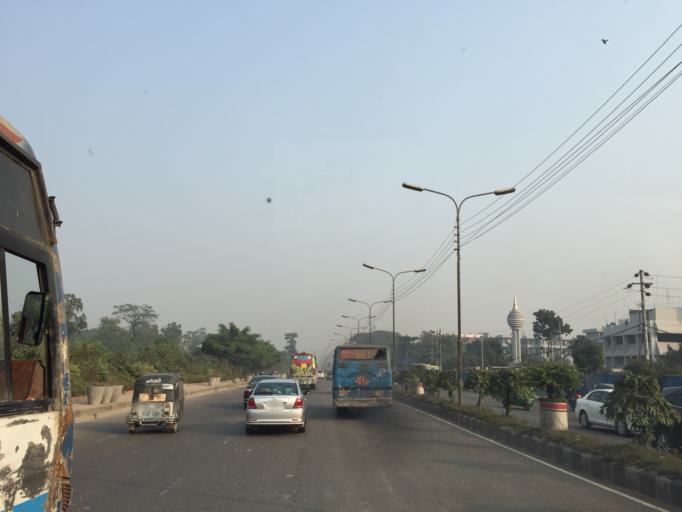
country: BD
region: Dhaka
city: Paltan
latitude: 23.7997
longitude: 90.4018
